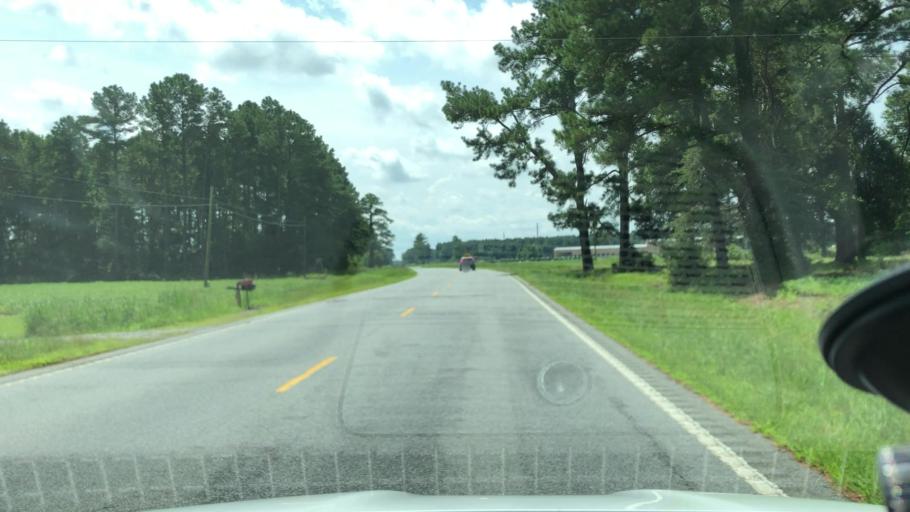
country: US
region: North Carolina
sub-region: Beaufort County
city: Washington
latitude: 35.6548
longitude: -77.0716
